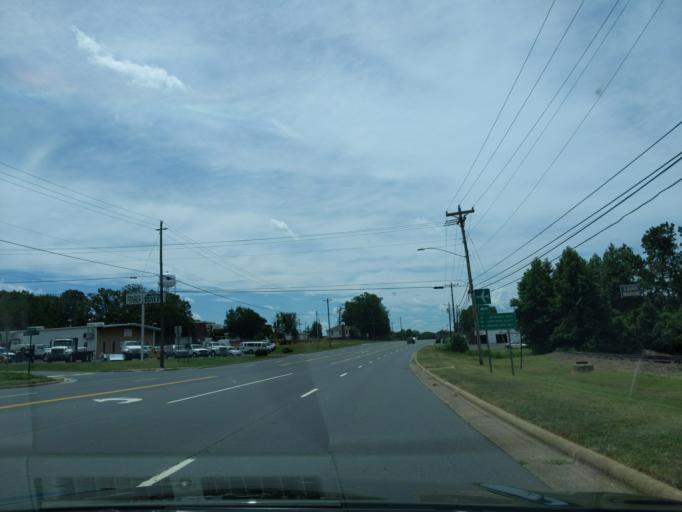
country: US
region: North Carolina
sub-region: Stanly County
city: Albemarle
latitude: 35.4021
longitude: -80.2010
